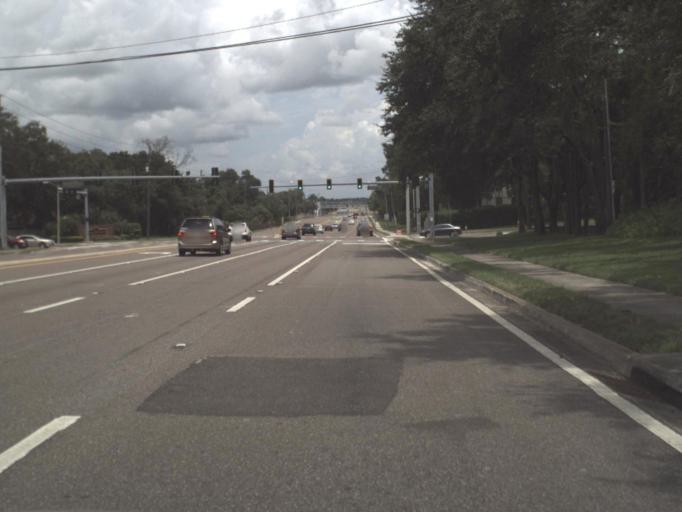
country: US
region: Florida
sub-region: Pinellas County
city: Saint George
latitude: 28.0489
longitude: -82.7194
